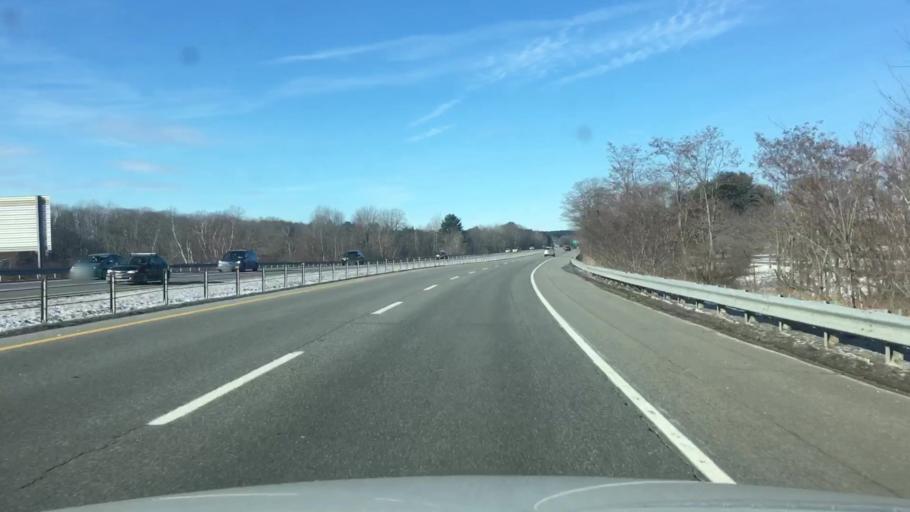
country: US
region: Maine
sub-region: Cumberland County
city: Brunswick
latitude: 43.9118
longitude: -69.9373
